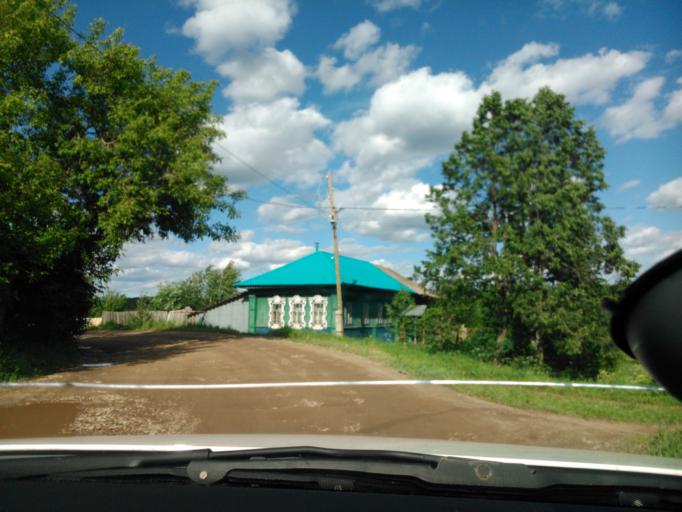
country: RU
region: Perm
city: Ust'-Kachka
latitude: 57.9455
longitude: 55.7451
